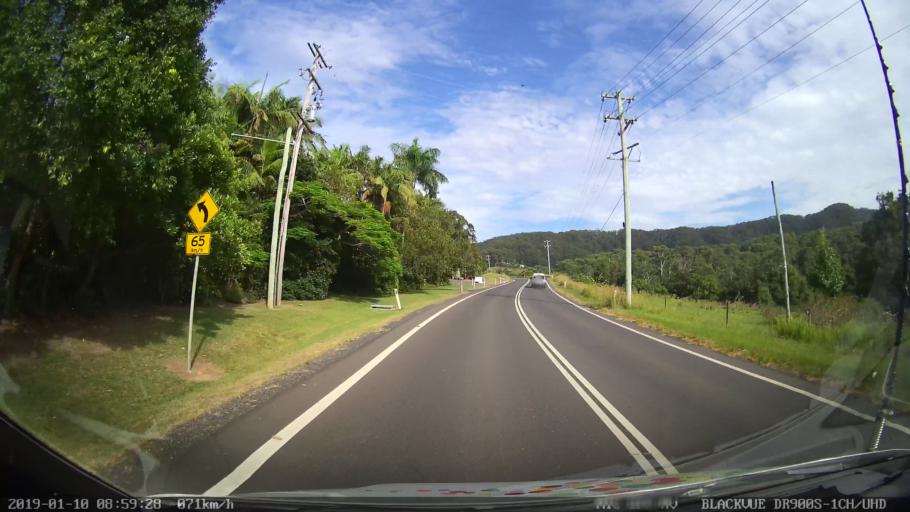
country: AU
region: New South Wales
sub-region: Coffs Harbour
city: Coffs Harbour
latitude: -30.2851
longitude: 153.0783
